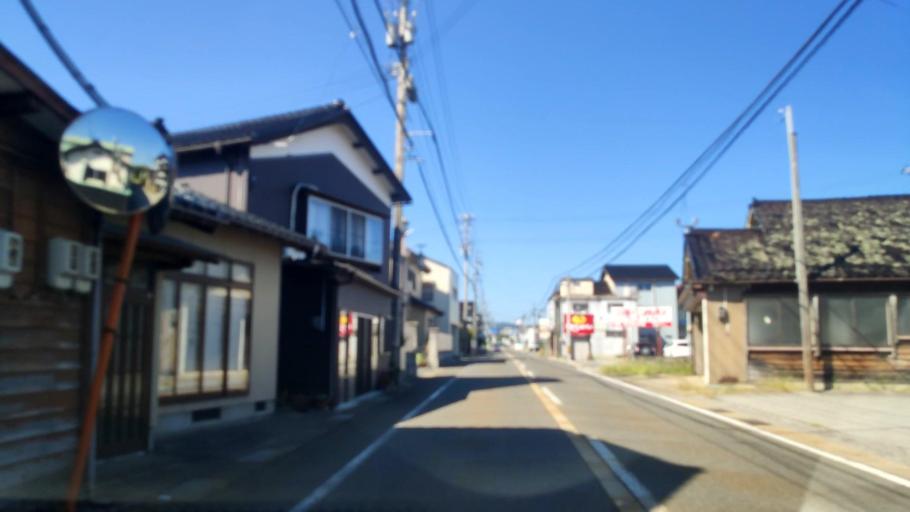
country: JP
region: Ishikawa
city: Nanao
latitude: 37.4413
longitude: 137.2648
